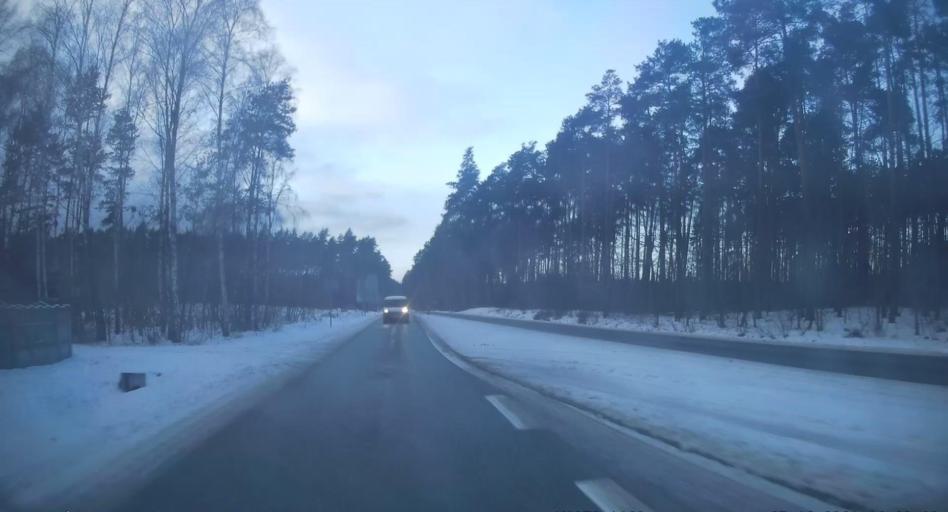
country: PL
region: Swietokrzyskie
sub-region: Powiat konecki
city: Radoszyce
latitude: 51.1027
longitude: 20.3137
